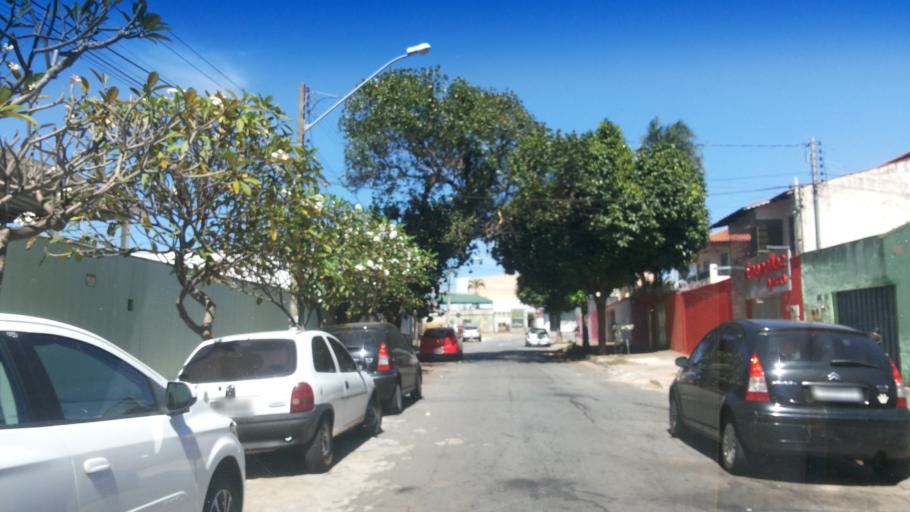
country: BR
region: Goias
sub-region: Goiania
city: Goiania
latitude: -16.7193
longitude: -49.2594
